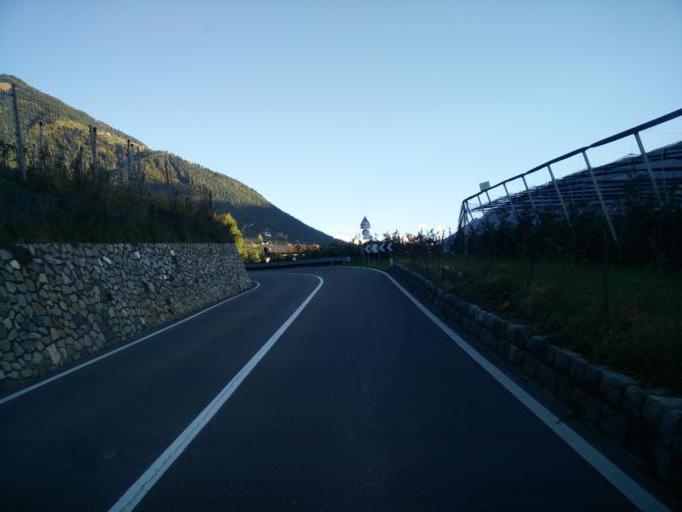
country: IT
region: Trentino-Alto Adige
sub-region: Bolzano
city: Caines
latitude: 46.6895
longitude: 11.1706
